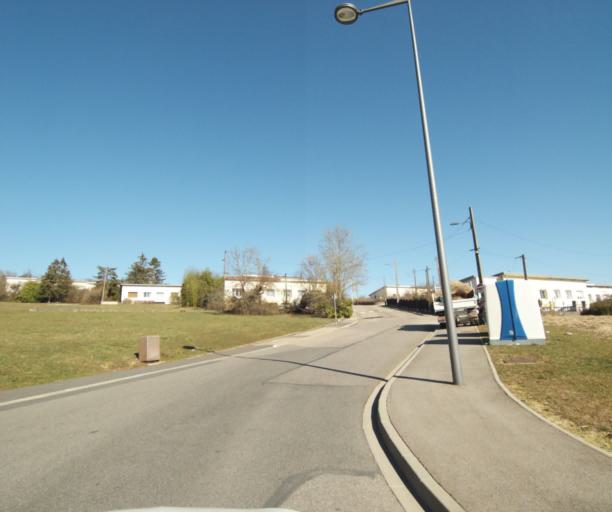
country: FR
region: Lorraine
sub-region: Departement de Meurthe-et-Moselle
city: Saint-Max
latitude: 48.7053
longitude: 6.1955
